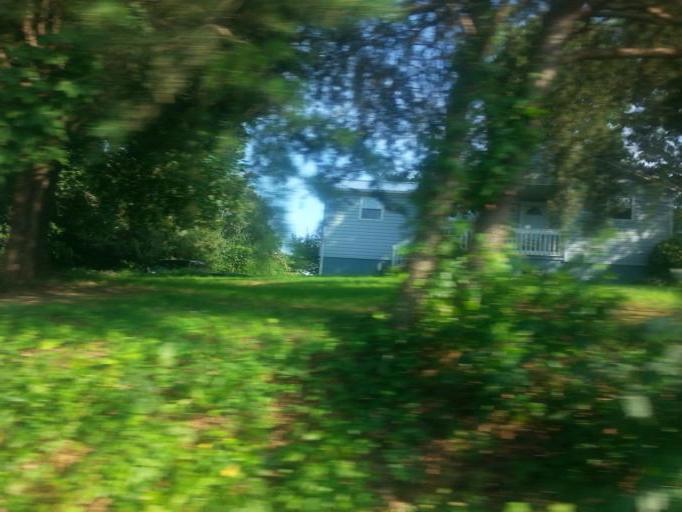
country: US
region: Tennessee
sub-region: Blount County
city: Wildwood
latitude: 35.8170
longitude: -83.8264
